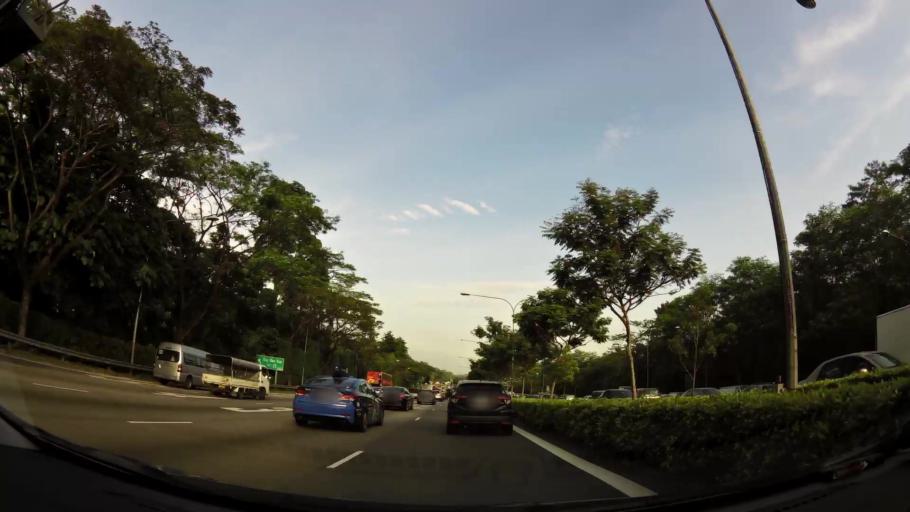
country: SG
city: Singapore
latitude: 1.3356
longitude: 103.8103
